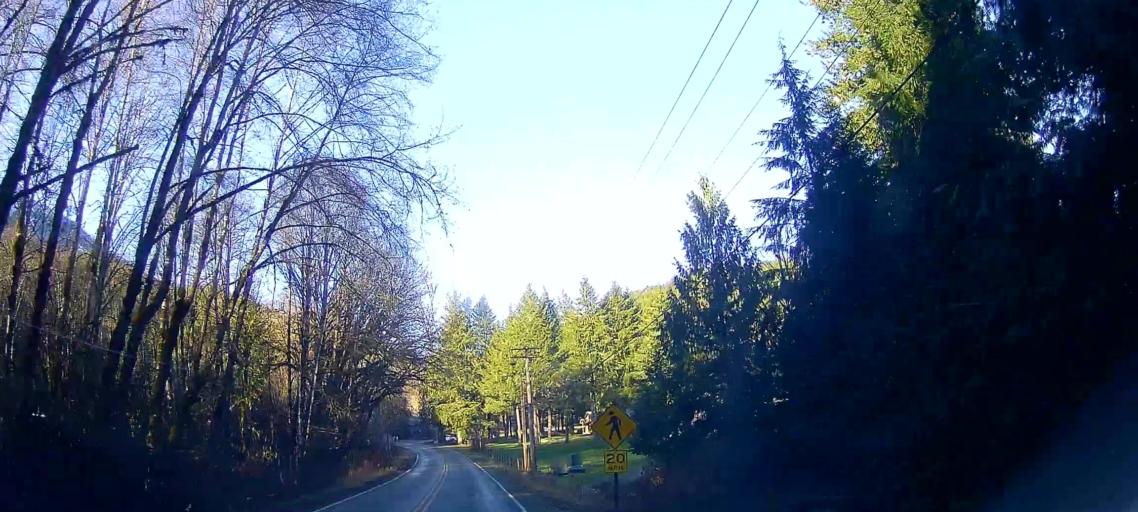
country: US
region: Washington
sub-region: Snohomish County
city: Darrington
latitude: 48.5772
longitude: -121.7737
